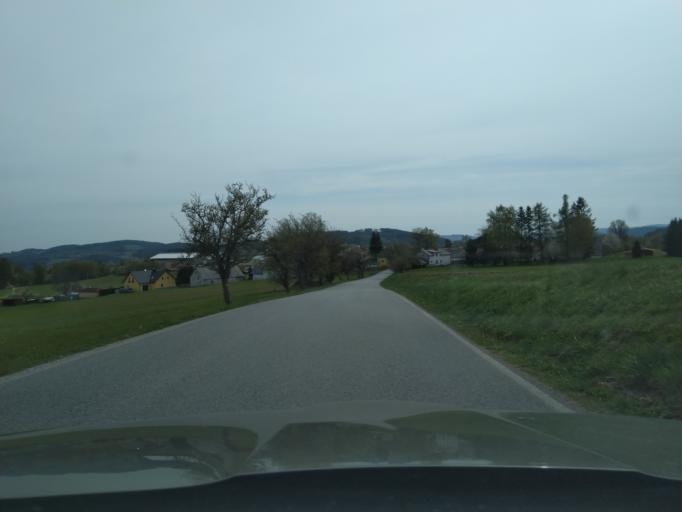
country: CZ
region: Jihocesky
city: Vacov
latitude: 49.1432
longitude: 13.7131
